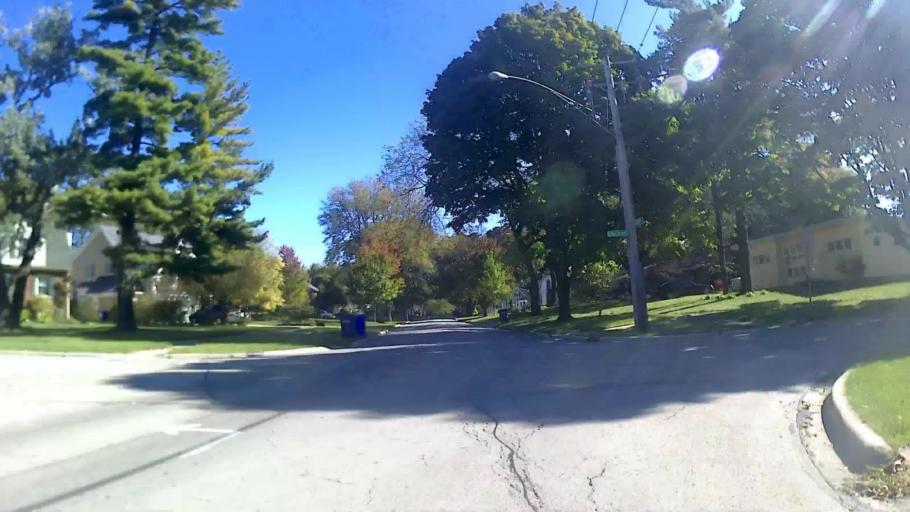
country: US
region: Illinois
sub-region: DuPage County
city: Wheaton
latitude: 41.8622
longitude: -88.0847
